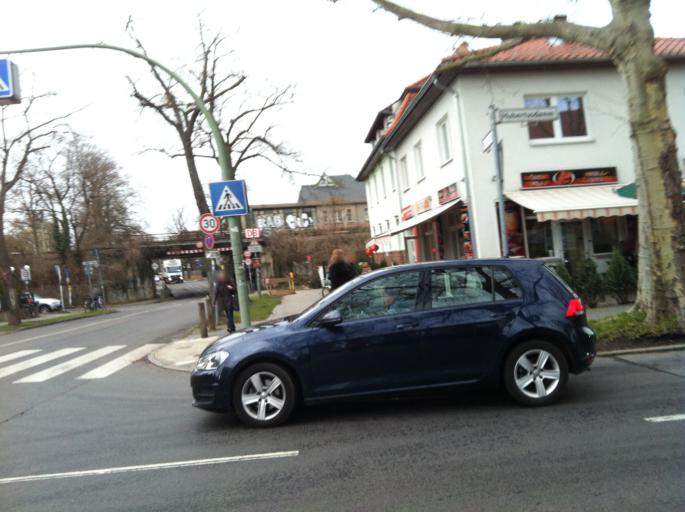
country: DE
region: Berlin
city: Karow
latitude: 52.6143
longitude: 13.4697
